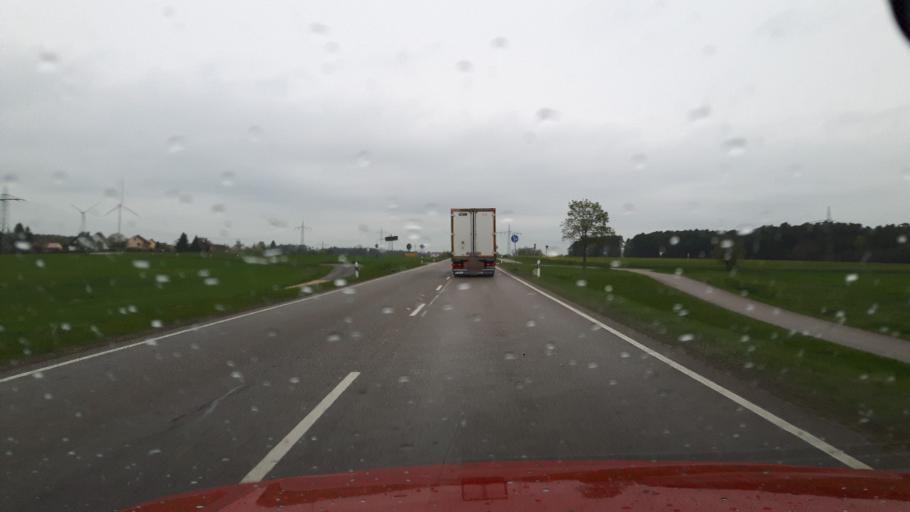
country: DE
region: Bavaria
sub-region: Regierungsbezirk Mittelfranken
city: Burgoberbach
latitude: 49.2463
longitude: 10.5992
